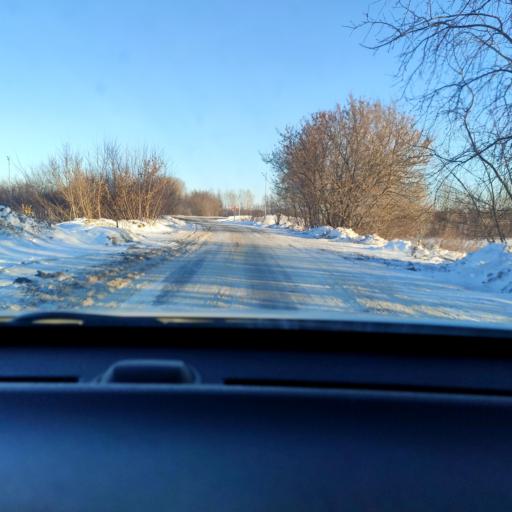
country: RU
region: Tatarstan
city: Stolbishchi
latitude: 55.6433
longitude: 49.2885
